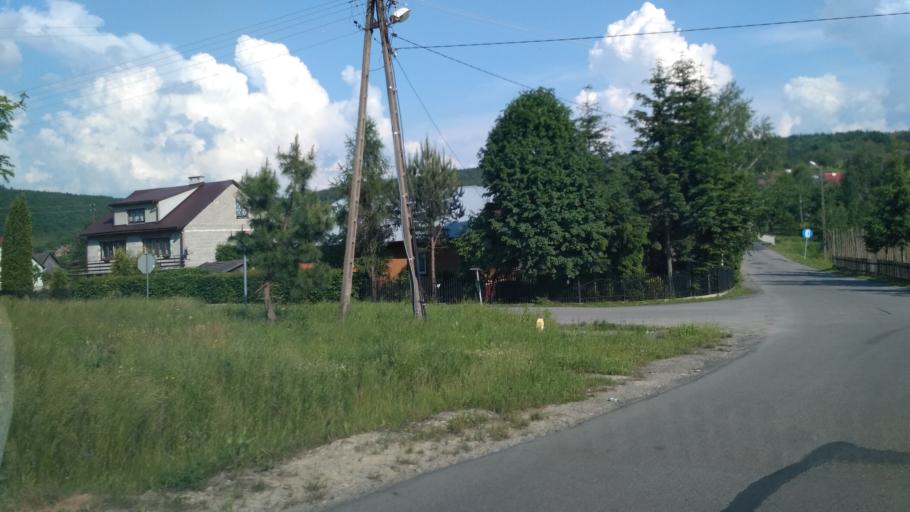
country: PL
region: Subcarpathian Voivodeship
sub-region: Powiat jaroslawski
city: Kramarzowka
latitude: 49.8662
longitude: 22.5126
